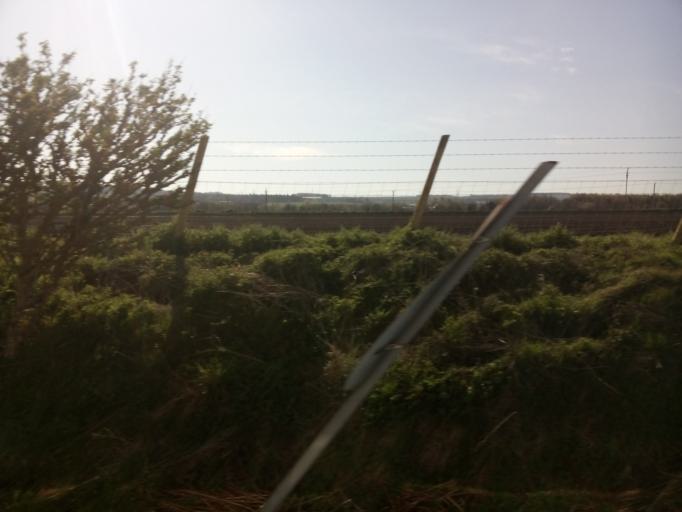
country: GB
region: Scotland
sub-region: East Lothian
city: Musselburgh
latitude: 55.9307
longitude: -3.0446
